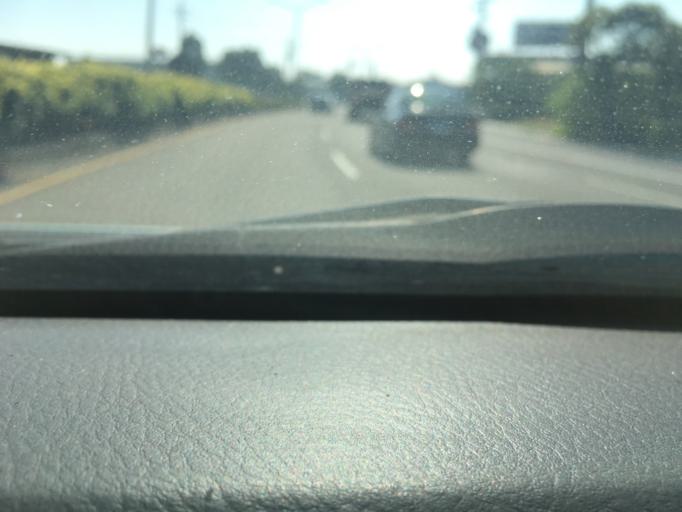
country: TW
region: Taiwan
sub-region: Hsinchu
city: Hsinchu
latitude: 24.8211
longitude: 120.9269
